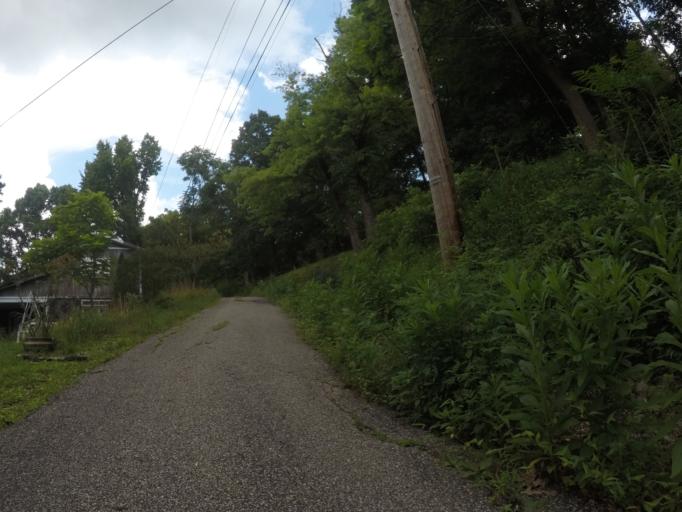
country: US
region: West Virginia
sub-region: Cabell County
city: Huntington
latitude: 38.4222
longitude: -82.3835
